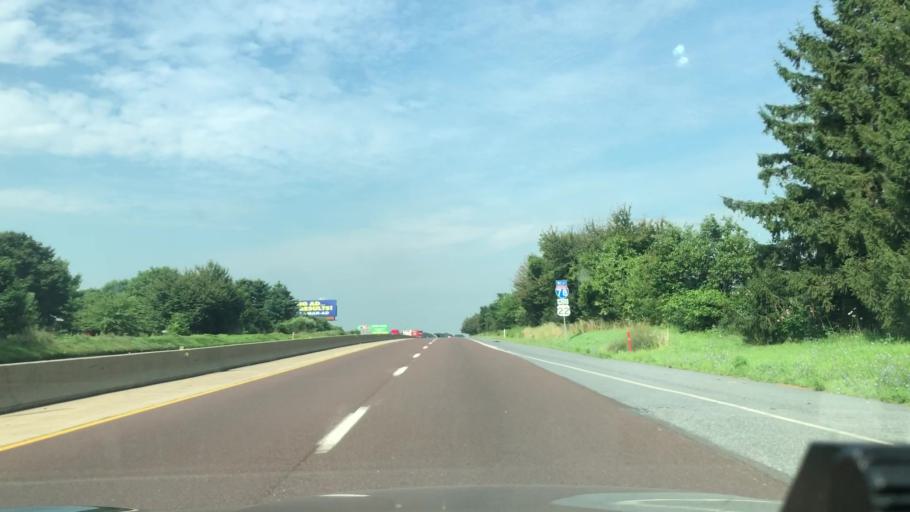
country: US
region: Pennsylvania
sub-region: Lebanon County
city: Myerstown
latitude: 40.4829
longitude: -76.2598
